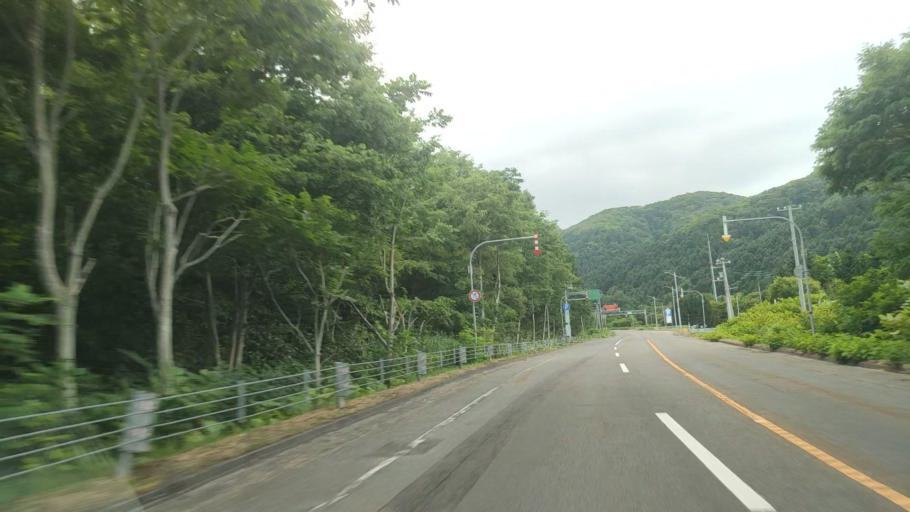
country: JP
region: Hokkaido
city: Rumoi
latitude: 43.8280
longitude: 141.4738
